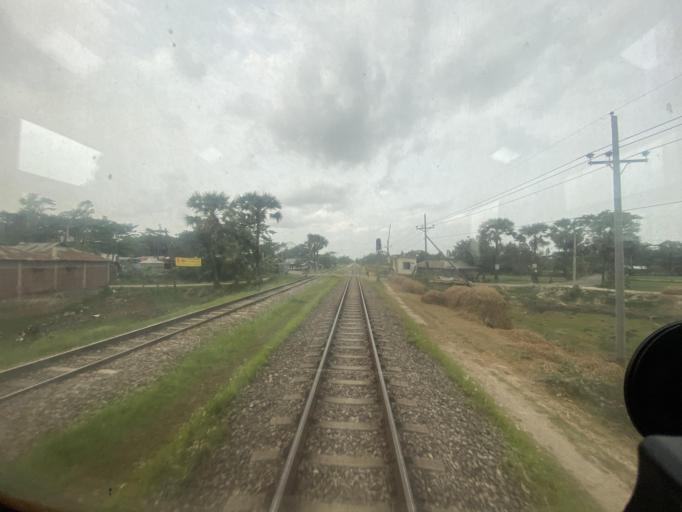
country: BD
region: Chittagong
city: Laksham
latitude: 23.2075
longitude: 91.1514
